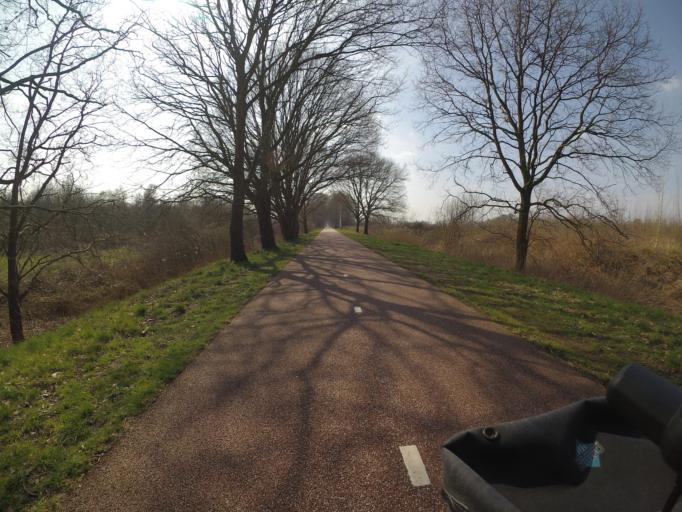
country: NL
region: North Brabant
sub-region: Gemeente Goirle
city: Goirle
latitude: 51.5348
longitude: 5.0292
